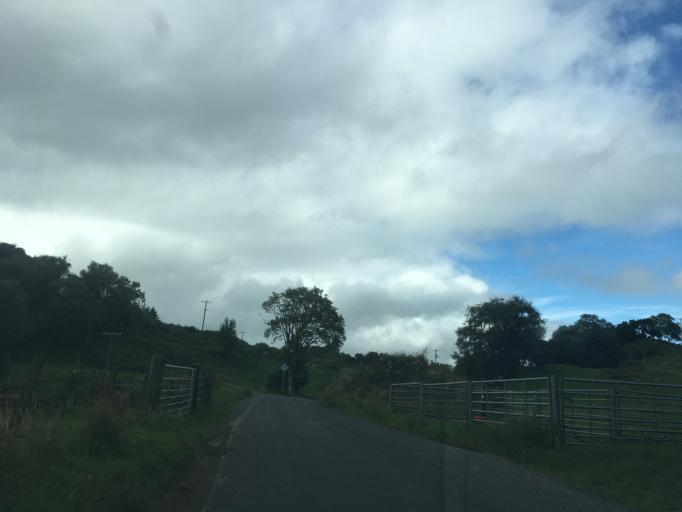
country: GB
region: Scotland
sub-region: Argyll and Bute
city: Ardrishaig
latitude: 56.0862
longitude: -5.5601
